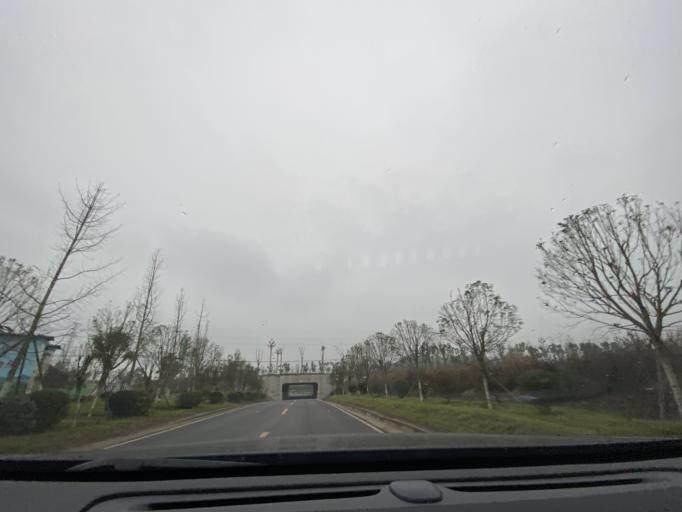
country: CN
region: Sichuan
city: Jiancheng
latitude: 30.3938
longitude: 104.6342
